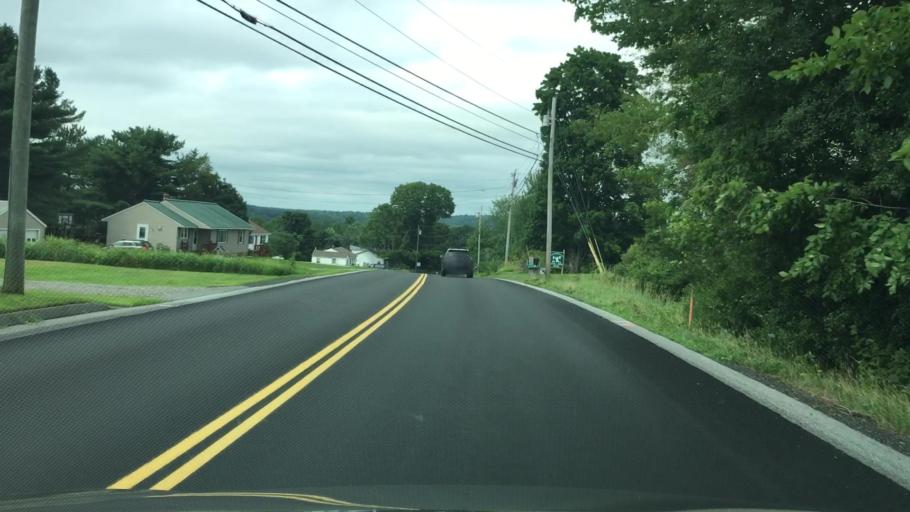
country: US
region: Maine
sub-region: Waldo County
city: Winterport
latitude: 44.6277
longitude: -68.8333
